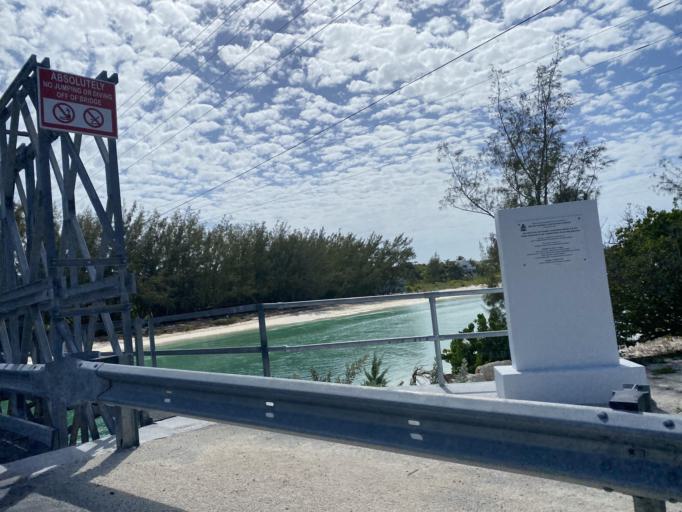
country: BS
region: Spanish Wells
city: Spanish Wells
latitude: 25.5480
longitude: -76.7714
